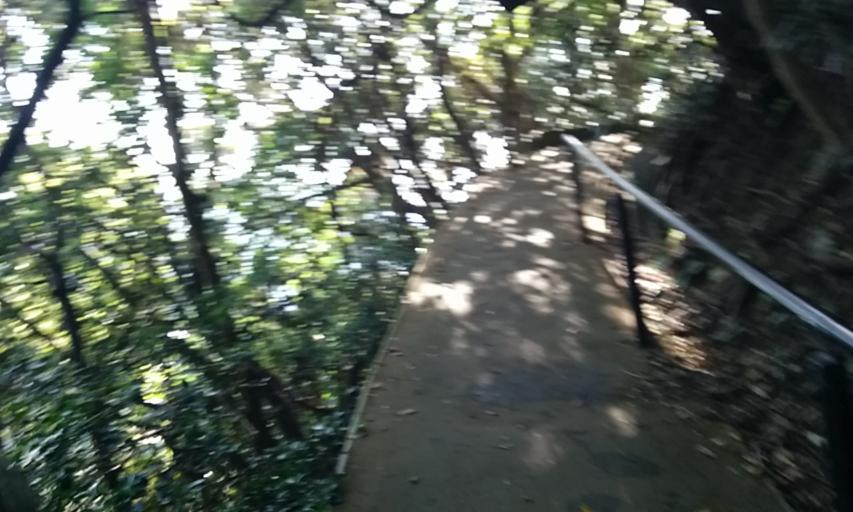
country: JP
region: Oita
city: Usuki
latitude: 33.3441
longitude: 132.0162
